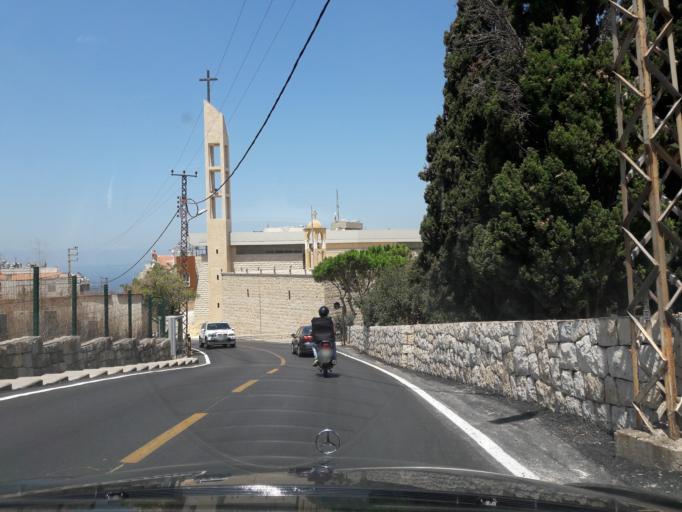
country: LB
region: Mont-Liban
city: Djounie
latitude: 33.9331
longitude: 35.6245
